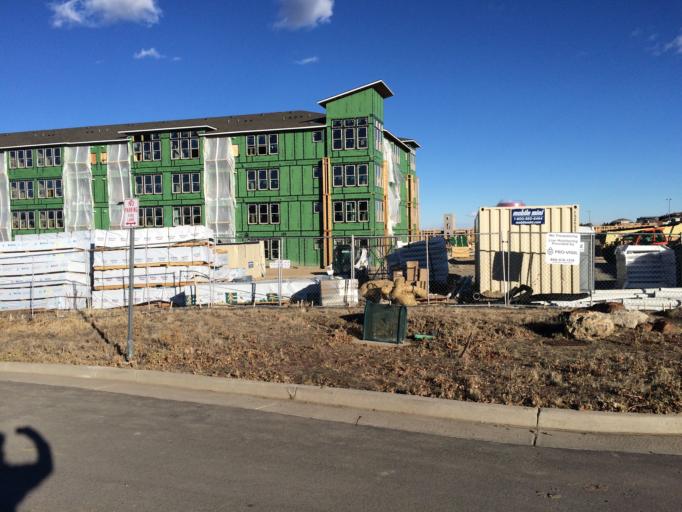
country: US
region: Colorado
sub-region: Boulder County
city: Superior
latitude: 39.9270
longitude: -105.1406
